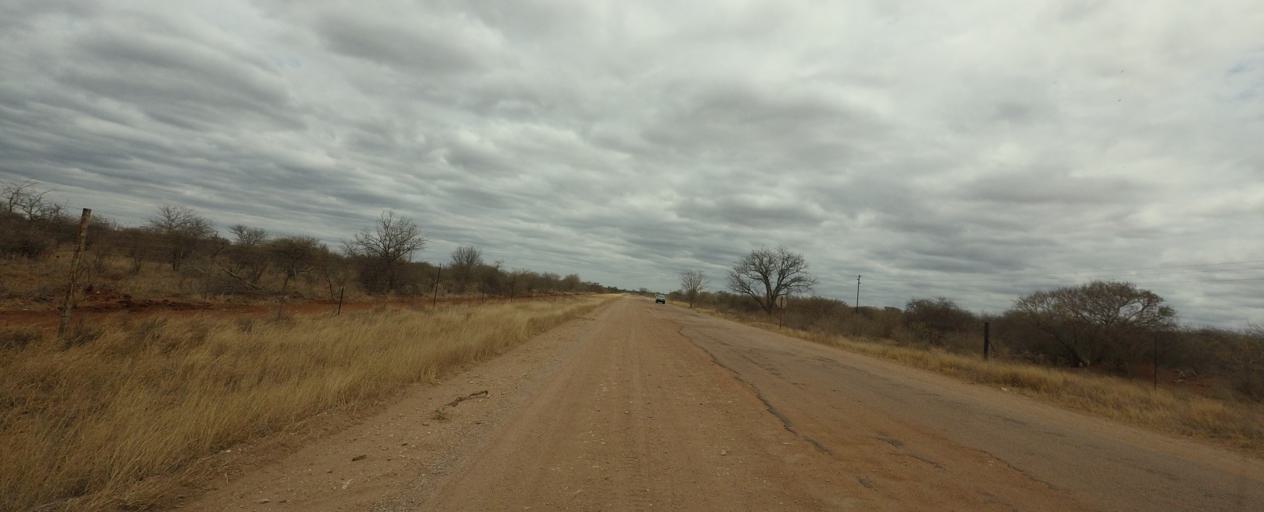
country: BW
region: Central
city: Mathathane
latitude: -22.7131
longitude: 28.5606
